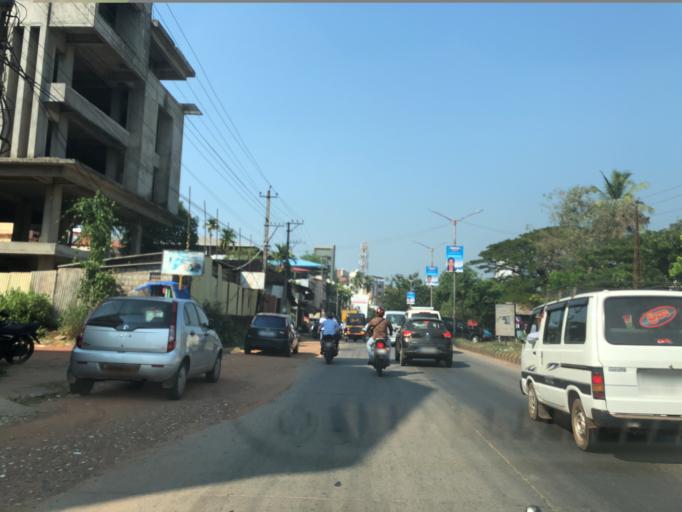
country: IN
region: Karnataka
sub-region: Dakshina Kannada
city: Mangalore
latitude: 12.9023
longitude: 74.8354
